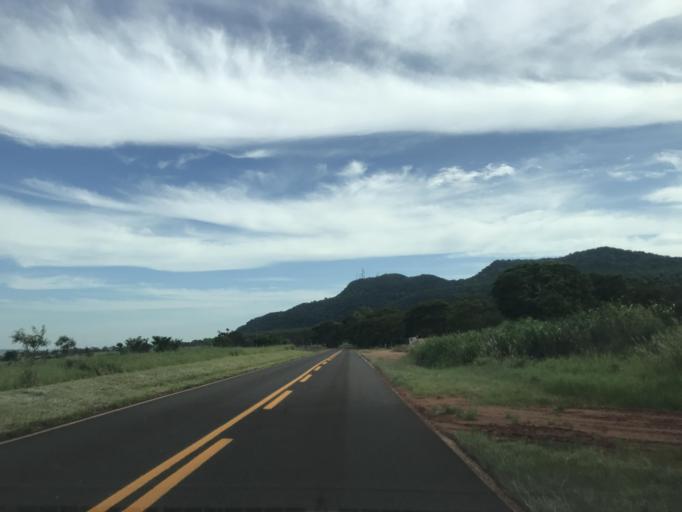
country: BR
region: Parana
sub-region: Terra Rica
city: Terra Rica
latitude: -22.8005
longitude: -52.6534
